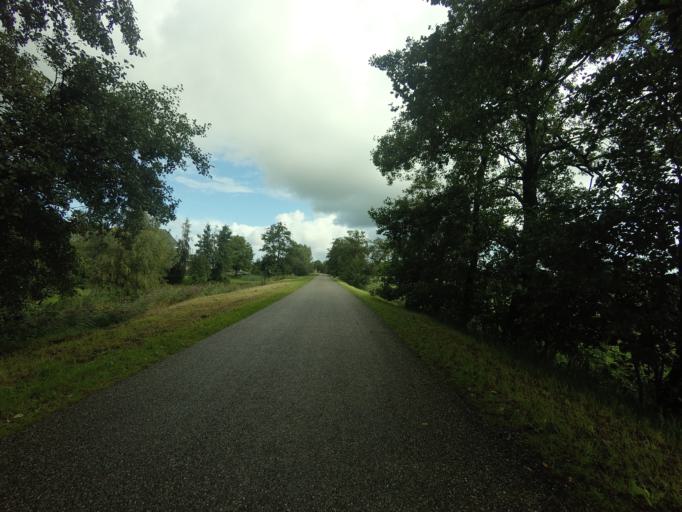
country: NL
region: Friesland
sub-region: Gemeente Tytsjerksteradiel
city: Garyp
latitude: 53.1523
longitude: 5.9494
